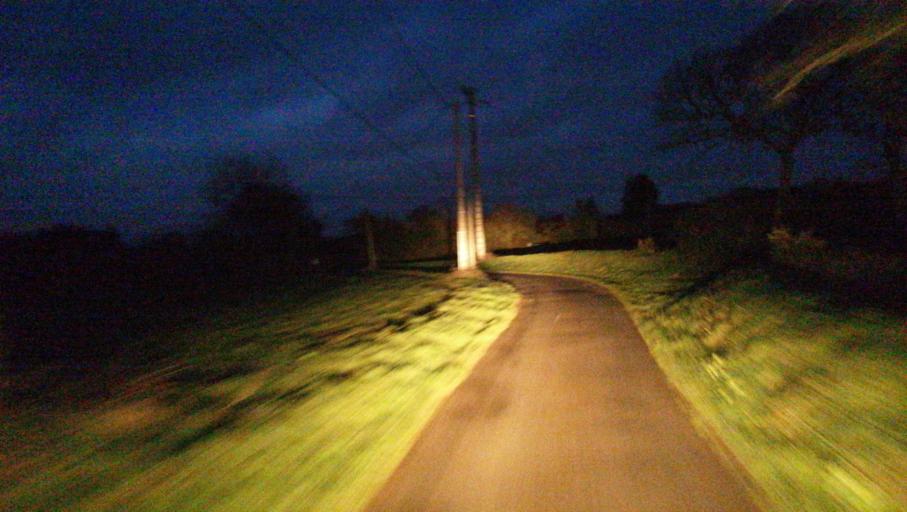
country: FR
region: Brittany
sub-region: Departement des Cotes-d'Armor
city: Plehedel
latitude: 48.6827
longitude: -3.0356
